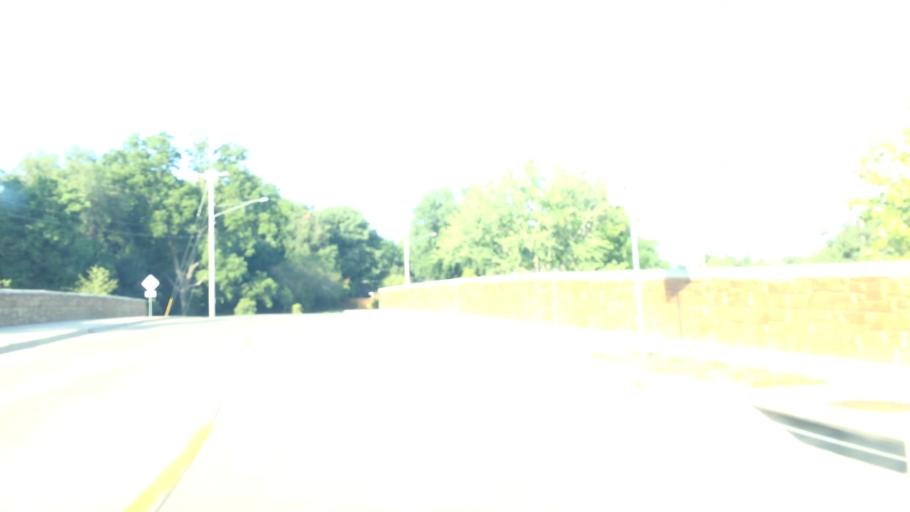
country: US
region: Missouri
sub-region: Greene County
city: Springfield
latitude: 37.1895
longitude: -93.2925
